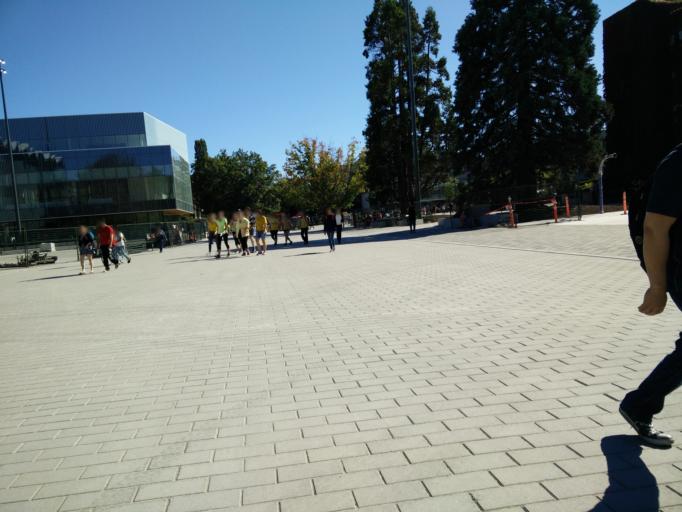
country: CA
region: British Columbia
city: West End
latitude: 49.2665
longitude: -123.2510
